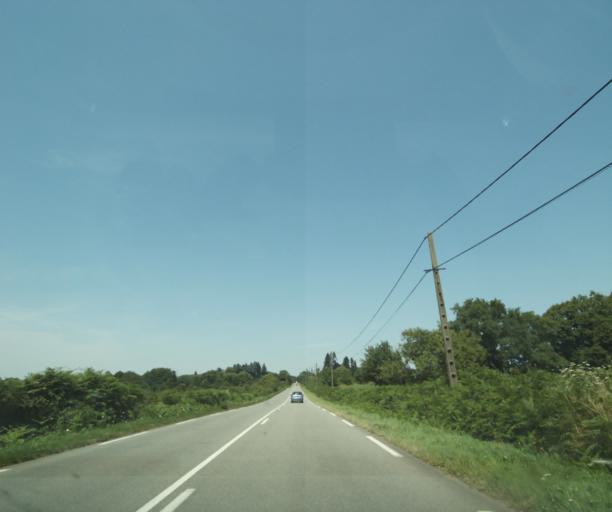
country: FR
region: Limousin
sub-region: Departement de la Haute-Vienne
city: Peyrilhac
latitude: 45.9665
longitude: 1.1644
